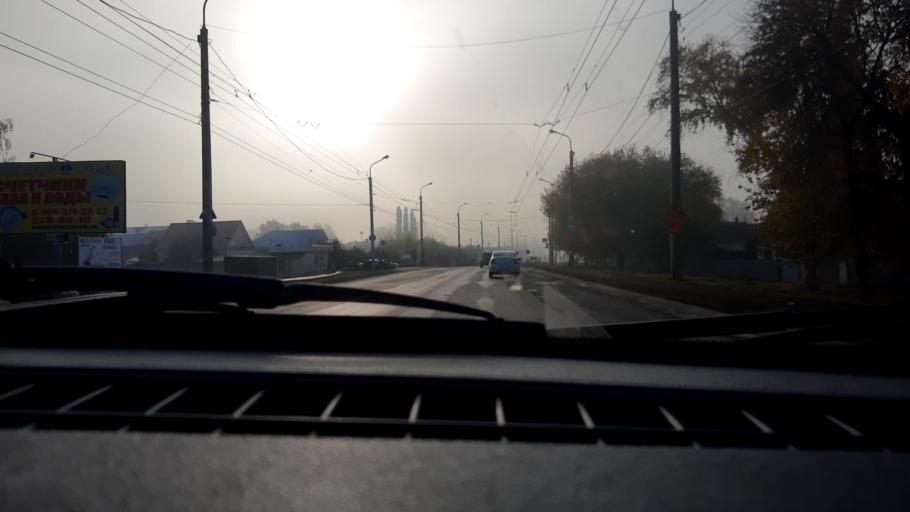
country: RU
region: Bashkortostan
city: Mikhaylovka
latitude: 54.7944
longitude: 55.8735
